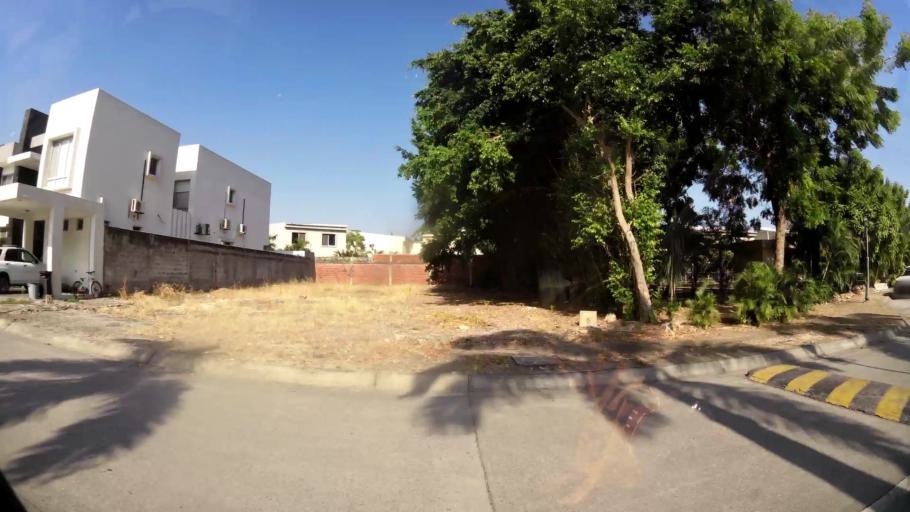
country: EC
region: Guayas
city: Santa Lucia
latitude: -2.1882
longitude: -79.9855
